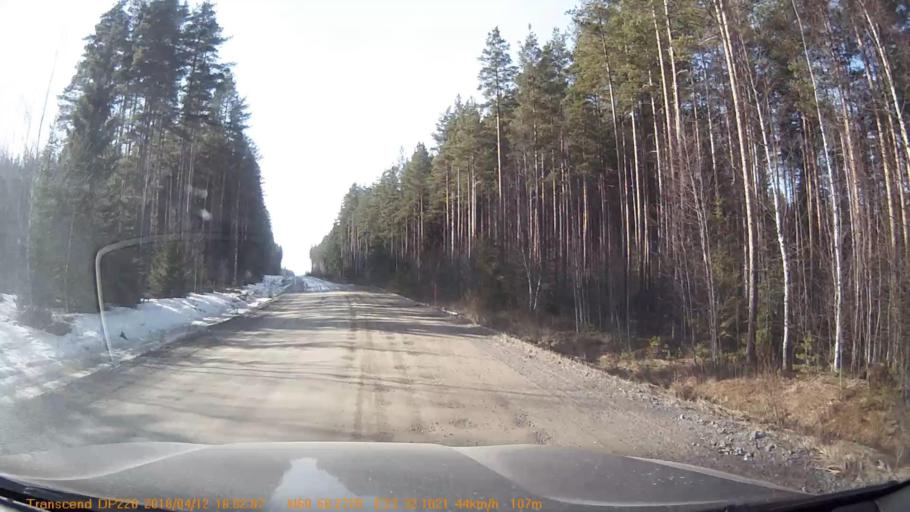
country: FI
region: Haeme
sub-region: Forssa
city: Jokioinen
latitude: 60.8381
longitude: 23.5342
